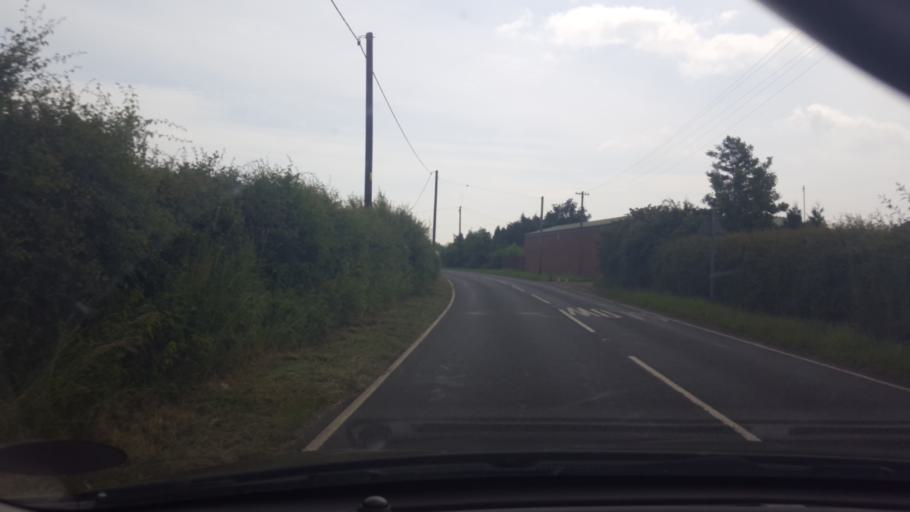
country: GB
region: England
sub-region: Essex
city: Mistley
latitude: 51.8930
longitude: 1.1036
